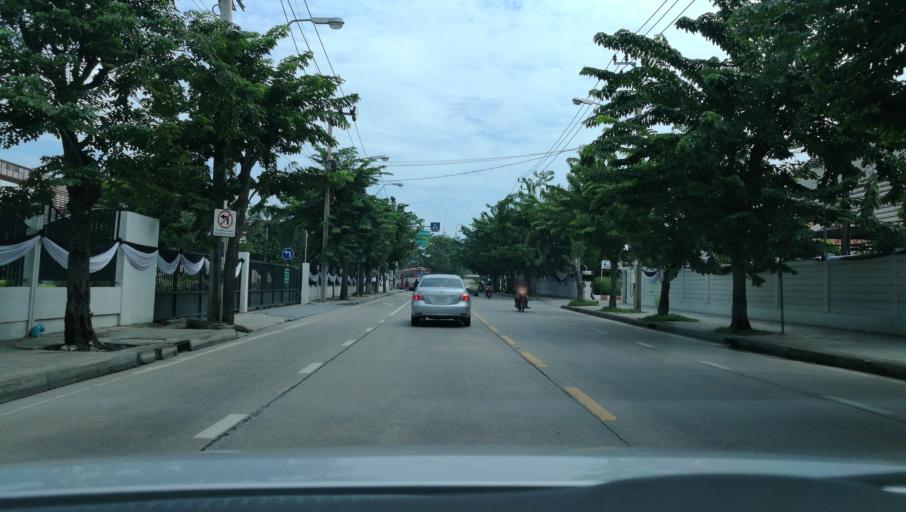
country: TH
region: Bangkok
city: Bang Sue
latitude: 13.8035
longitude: 100.5382
